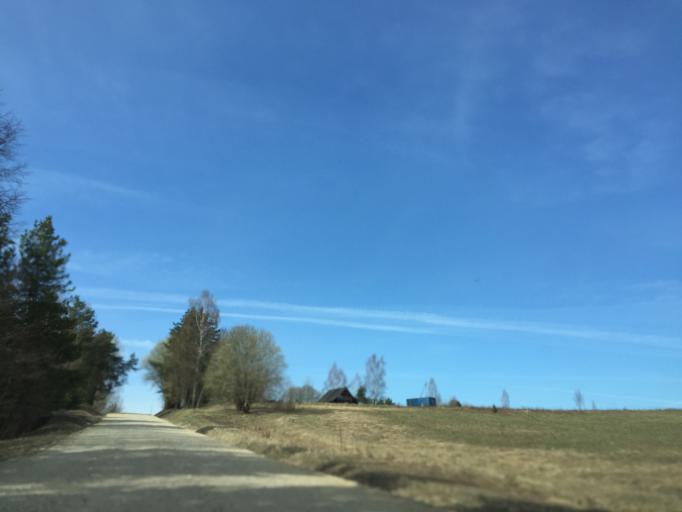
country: EE
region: Vorumaa
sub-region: Antsla vald
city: Vana-Antsla
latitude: 57.9479
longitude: 26.3746
